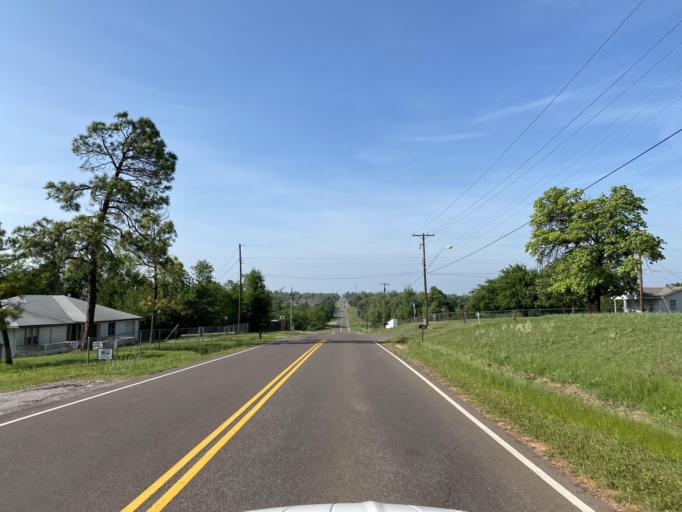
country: US
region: Oklahoma
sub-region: Oklahoma County
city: Nicoma Park
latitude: 35.4690
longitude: -97.3356
